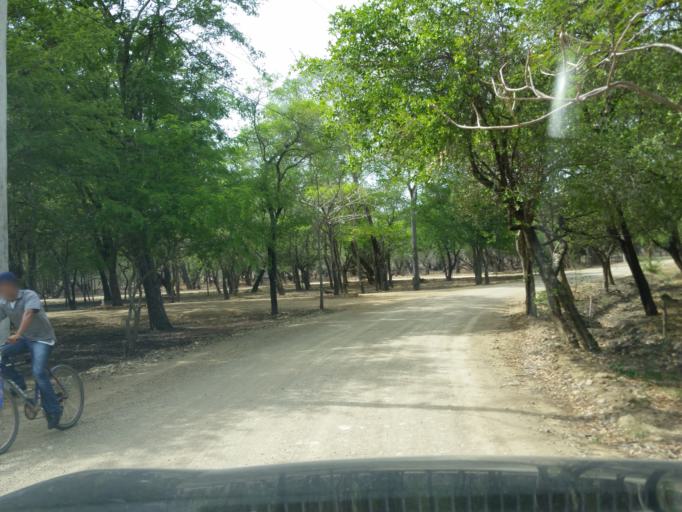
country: NI
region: Rivas
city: Tola
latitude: 11.4111
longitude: -86.0544
